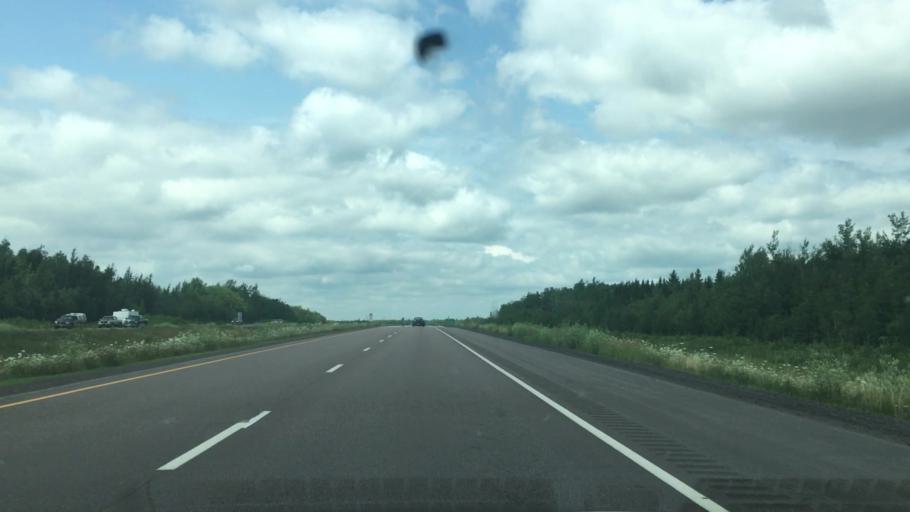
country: CA
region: New Brunswick
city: Dieppe
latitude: 46.1199
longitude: -64.6285
